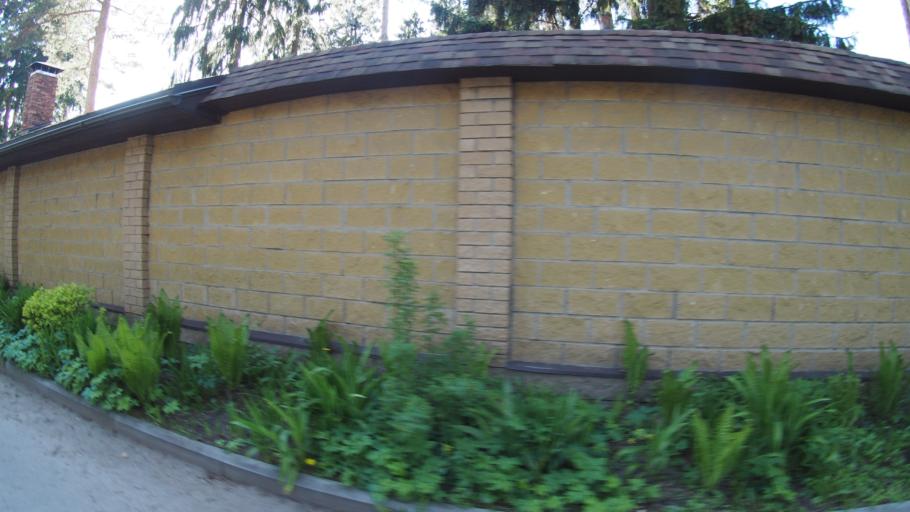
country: RU
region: Moskovskaya
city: Kratovo
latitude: 55.5730
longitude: 38.1789
